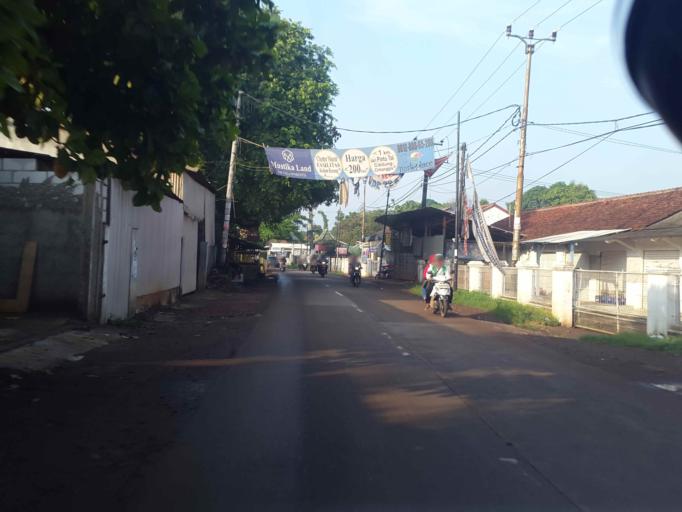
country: ID
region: West Java
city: Bekasi
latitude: -6.3271
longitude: 107.0526
